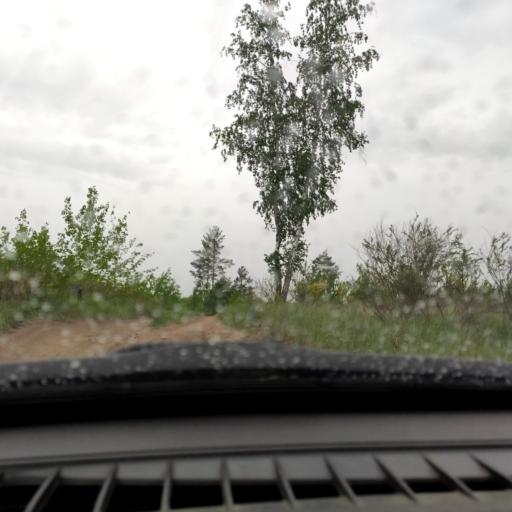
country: RU
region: Samara
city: Zhigulevsk
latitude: 53.5211
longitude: 49.5520
